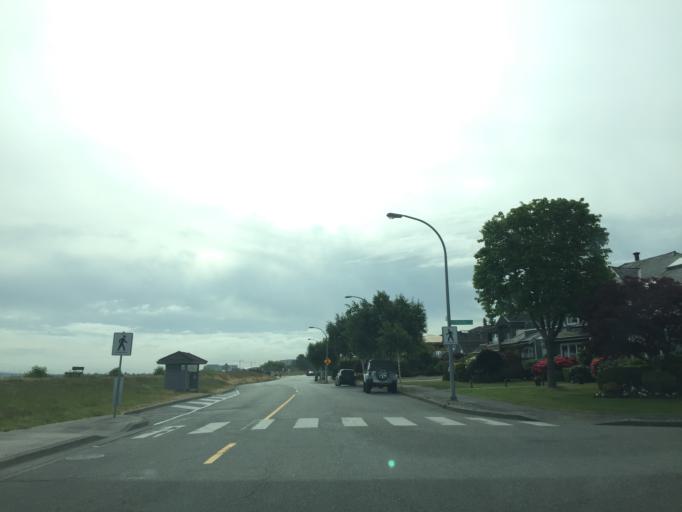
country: CA
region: British Columbia
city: Richmond
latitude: 49.1742
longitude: -123.1841
